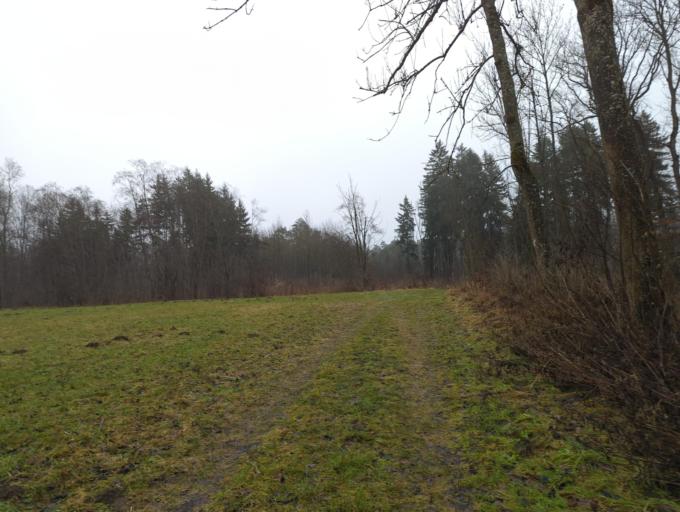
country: DE
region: Bavaria
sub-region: Swabia
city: Offingen
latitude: 48.4991
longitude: 10.3678
